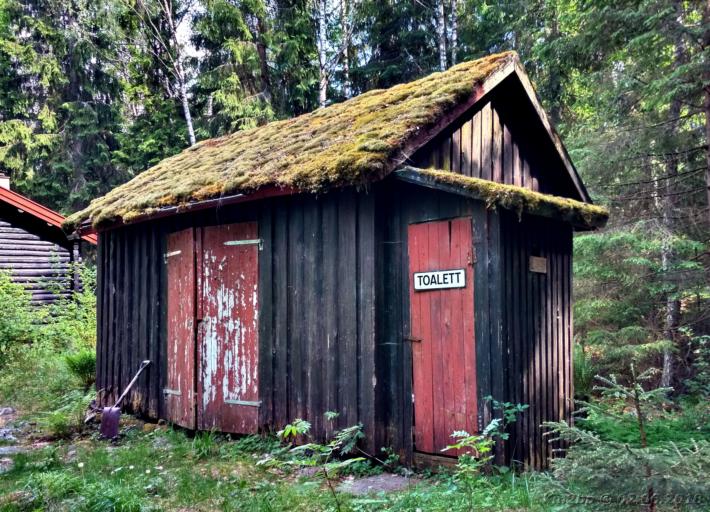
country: NO
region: Akershus
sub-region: Raelingen
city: Fjerdingby
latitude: 59.8898
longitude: 11.0678
